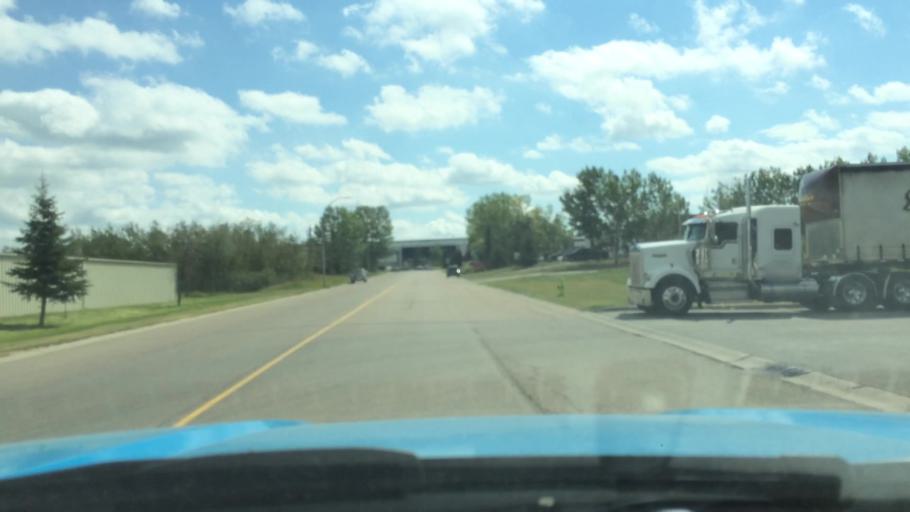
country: CA
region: Alberta
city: Airdrie
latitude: 51.2889
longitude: -113.9862
